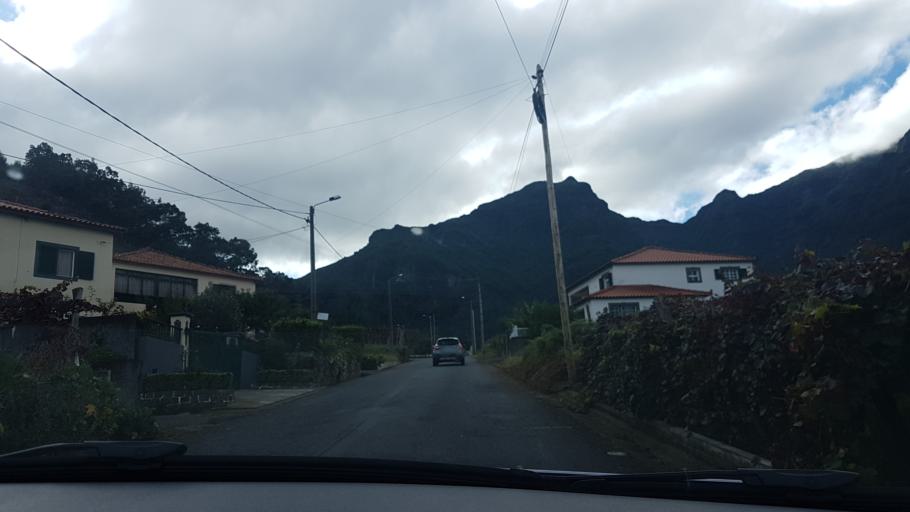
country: PT
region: Madeira
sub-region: Sao Vicente
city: Sao Vicente
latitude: 32.7789
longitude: -17.0293
